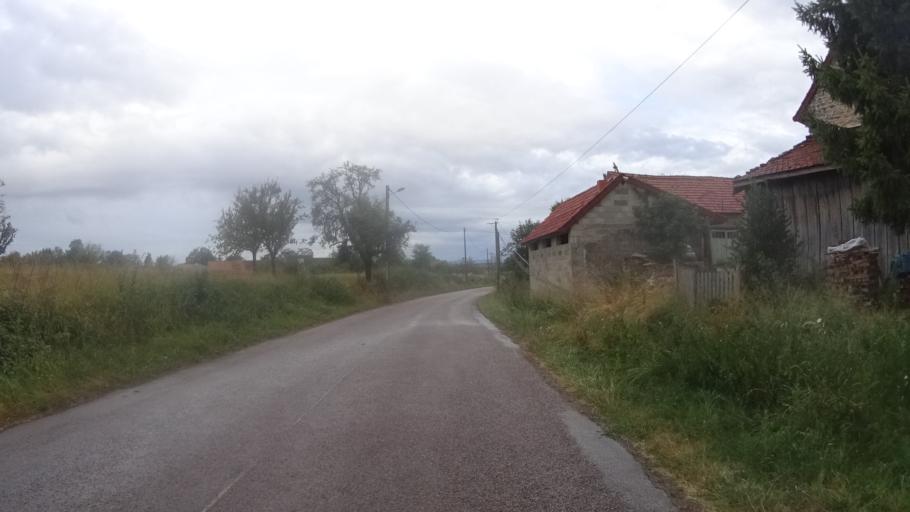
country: FR
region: Bourgogne
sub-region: Departement de Saone-et-Loire
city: Gergy
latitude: 46.9502
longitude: 4.9476
